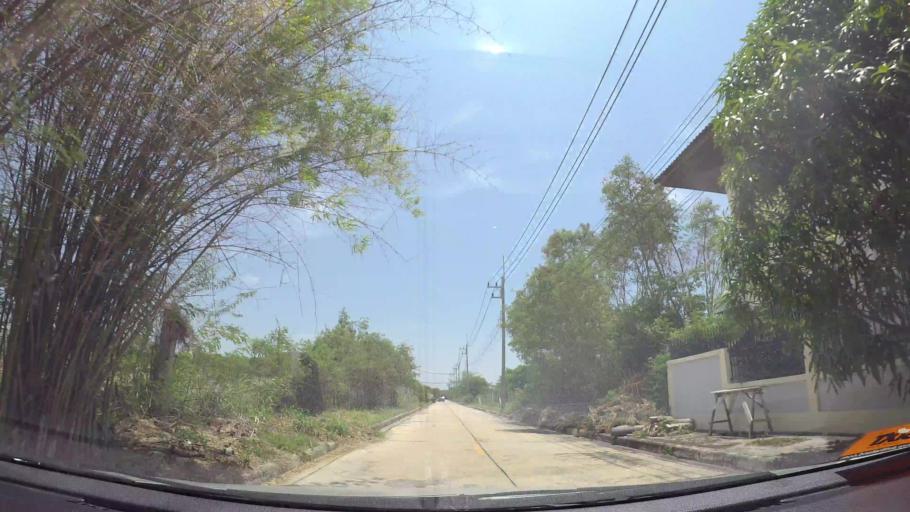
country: TH
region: Chon Buri
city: Chon Buri
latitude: 13.3382
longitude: 100.9455
